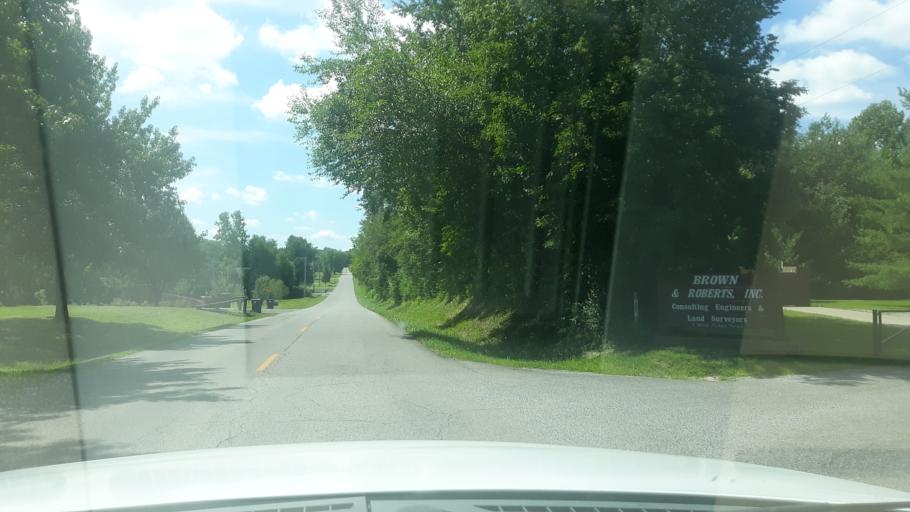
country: US
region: Illinois
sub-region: Saline County
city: Harrisburg
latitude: 37.7316
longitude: -88.5689
